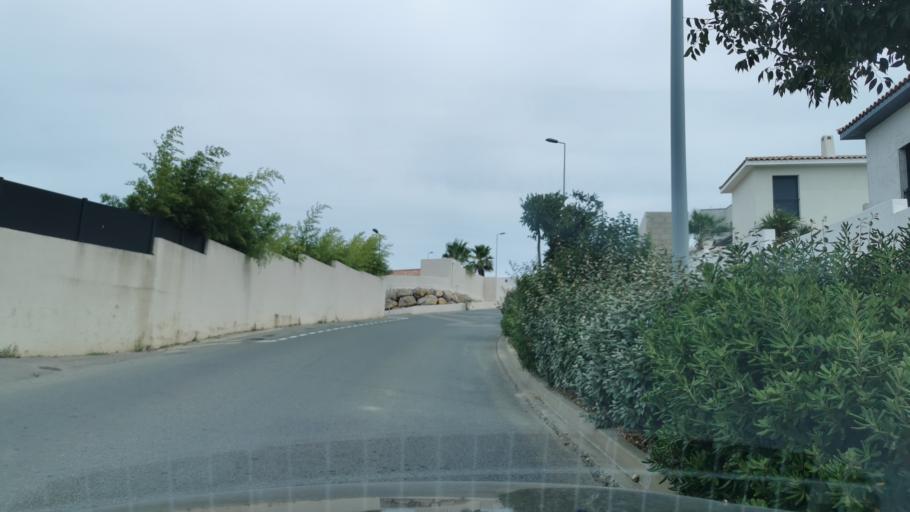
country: FR
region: Languedoc-Roussillon
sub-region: Departement de l'Aude
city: Narbonne
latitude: 43.1953
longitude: 2.9716
